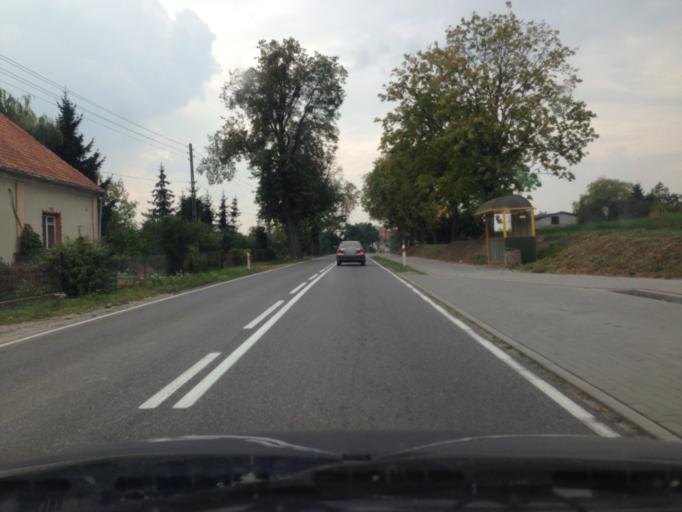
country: PL
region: Pomeranian Voivodeship
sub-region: Powiat kwidzynski
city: Kwidzyn
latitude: 53.7724
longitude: 18.9504
